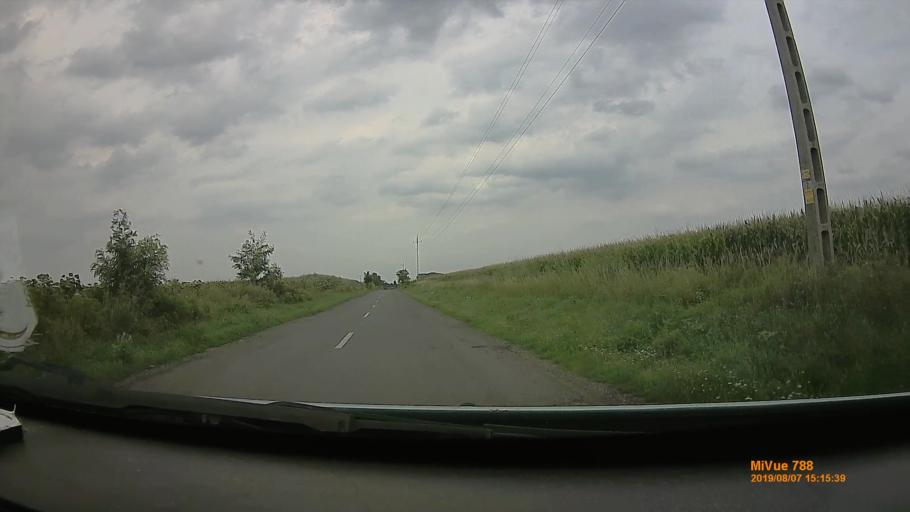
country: HU
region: Borsod-Abauj-Zemplen
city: Encs
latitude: 48.3405
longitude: 21.1311
